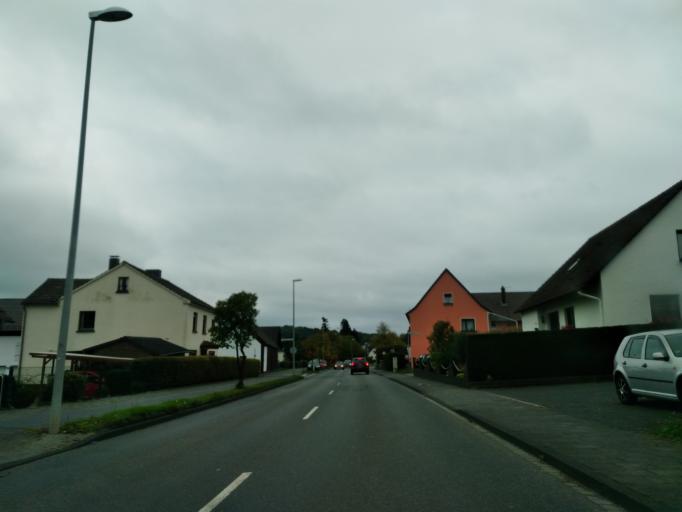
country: DE
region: Rheinland-Pfalz
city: Windhagen
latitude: 50.6576
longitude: 7.3019
